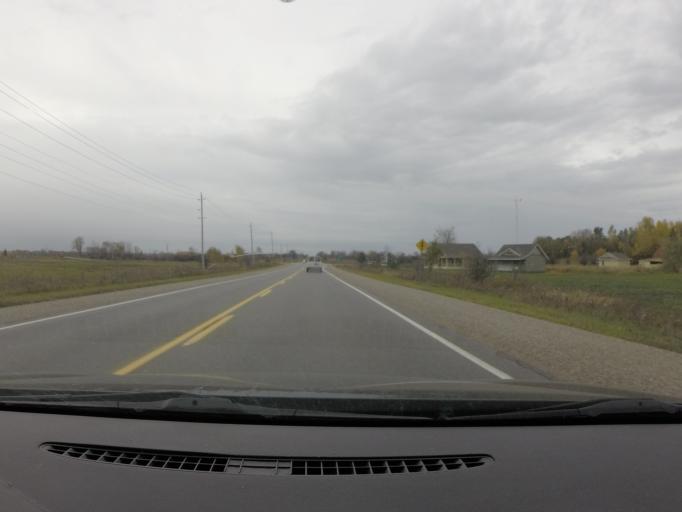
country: CA
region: Ontario
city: Perth
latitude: 44.9613
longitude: -76.2322
